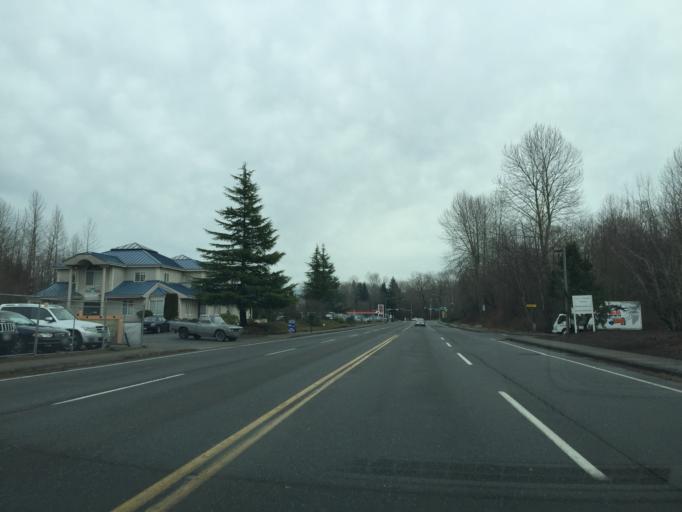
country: US
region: Washington
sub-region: Whatcom County
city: Marietta-Alderwood
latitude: 48.7860
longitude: -122.5238
